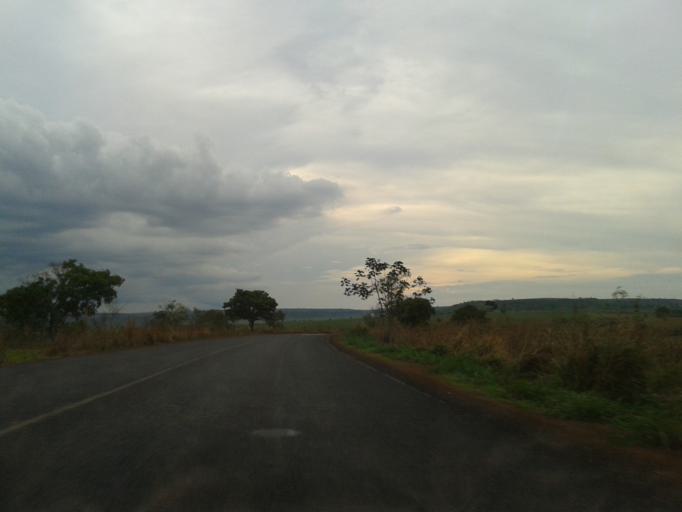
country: BR
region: Goias
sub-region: Quirinopolis
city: Quirinopolis
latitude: -18.1617
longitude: -50.4729
